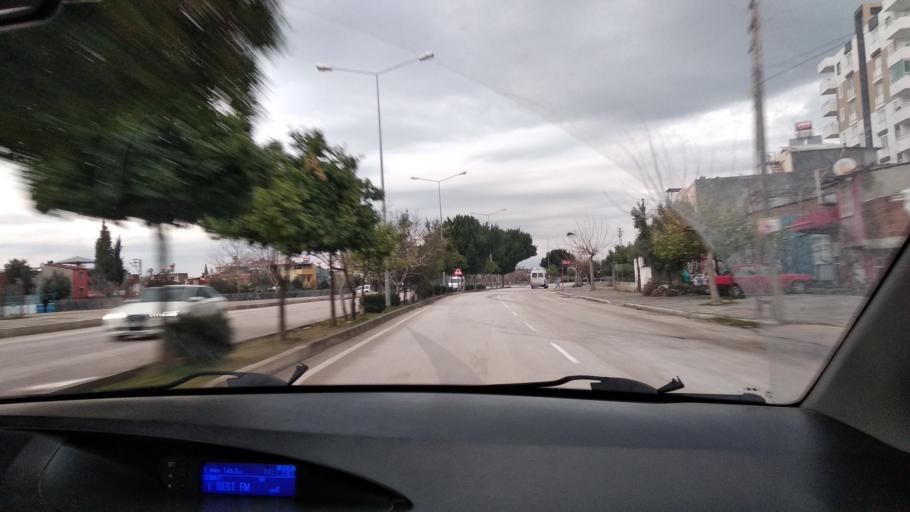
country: TR
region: Adana
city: Yuregir
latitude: 37.0109
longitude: 35.3891
